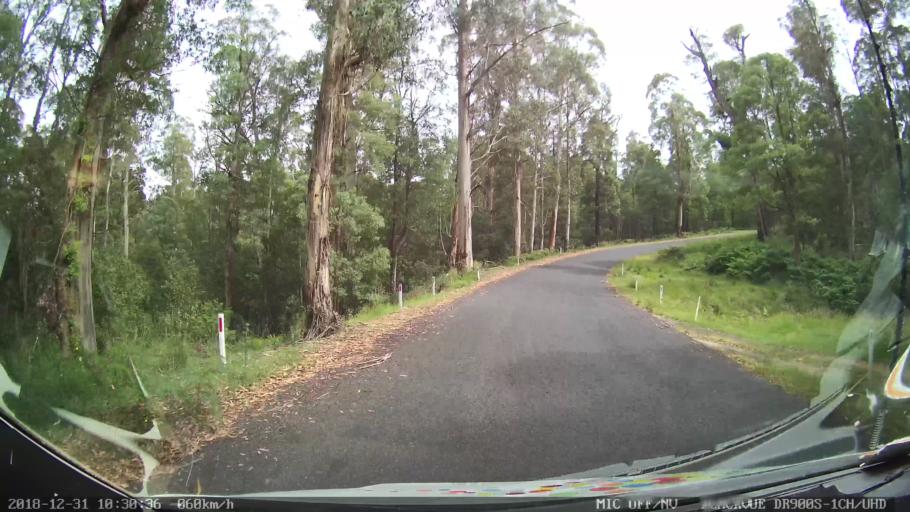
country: AU
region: New South Wales
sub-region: Snowy River
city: Jindabyne
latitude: -36.4617
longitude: 148.1507
